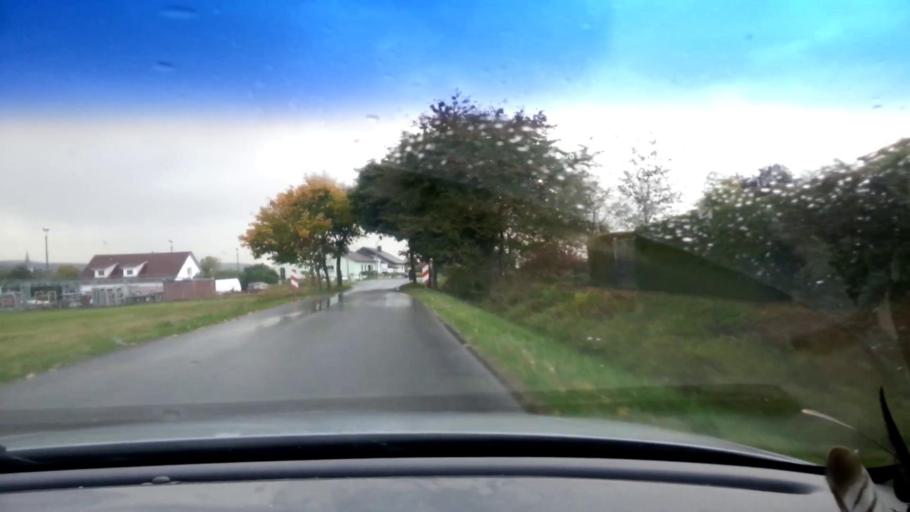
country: DE
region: Bavaria
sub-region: Upper Franconia
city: Burgebrach
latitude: 49.8471
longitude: 10.7370
